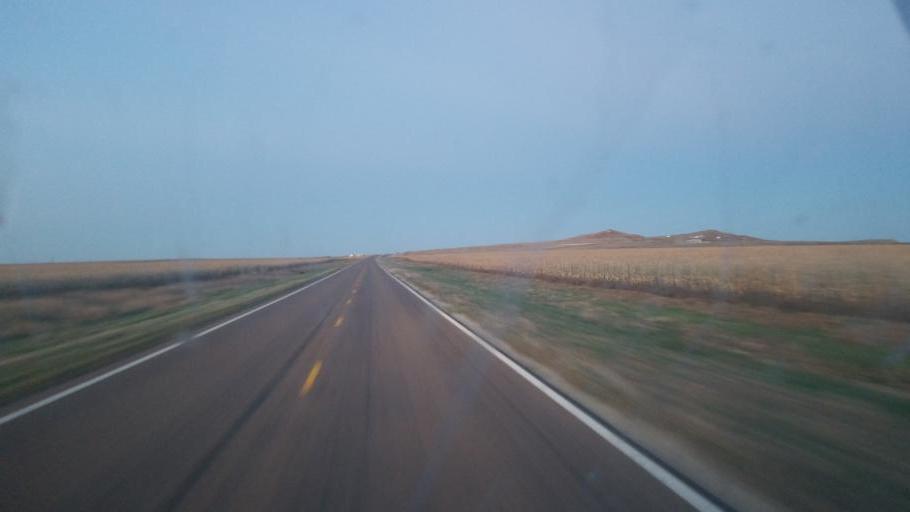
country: US
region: Kansas
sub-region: Wallace County
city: Sharon Springs
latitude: 39.0117
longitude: -101.3626
